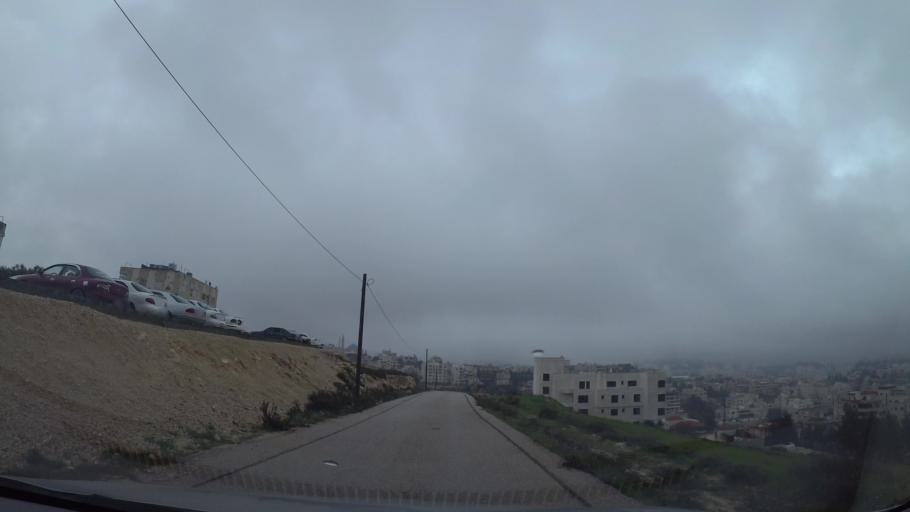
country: JO
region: Amman
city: Al Jubayhah
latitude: 32.0181
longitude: 35.8317
